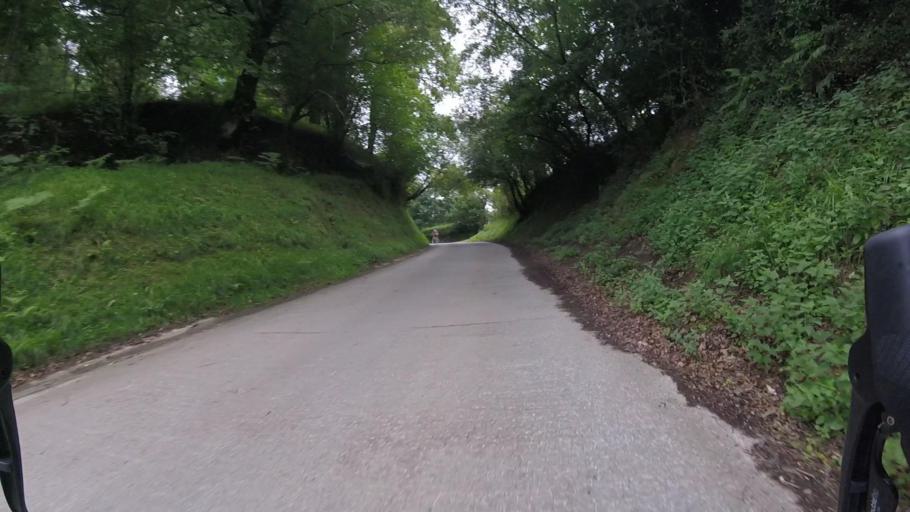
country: ES
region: Basque Country
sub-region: Provincia de Guipuzcoa
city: Errenteria
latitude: 43.2627
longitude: -1.8922
